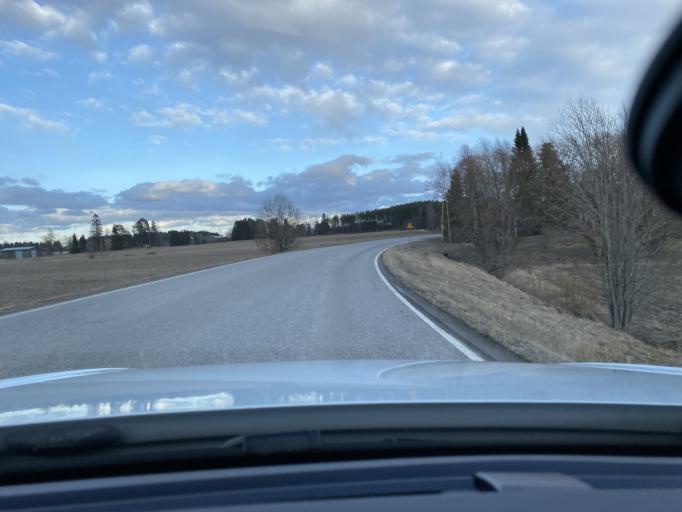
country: FI
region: Pirkanmaa
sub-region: Lounais-Pirkanmaa
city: Punkalaidun
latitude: 61.1206
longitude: 23.0683
